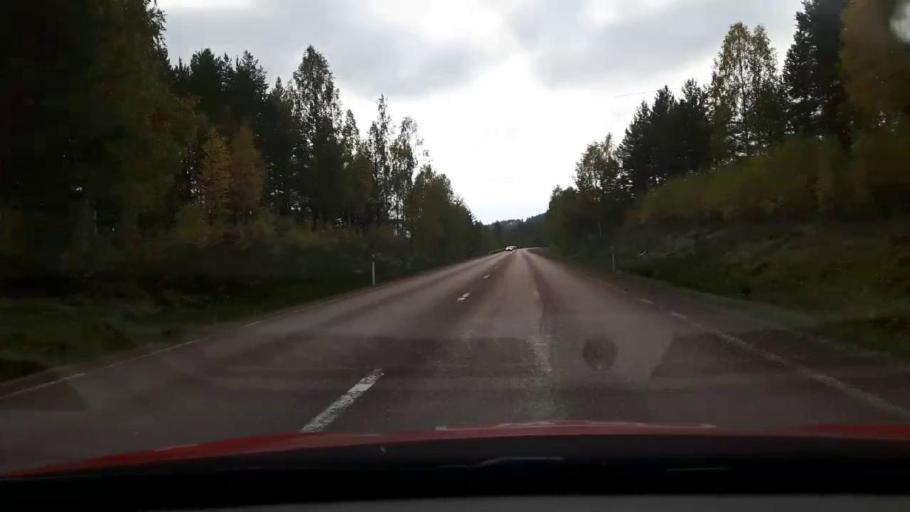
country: SE
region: Gaevleborg
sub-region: Bollnas Kommun
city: Arbra
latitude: 61.6072
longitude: 16.2956
